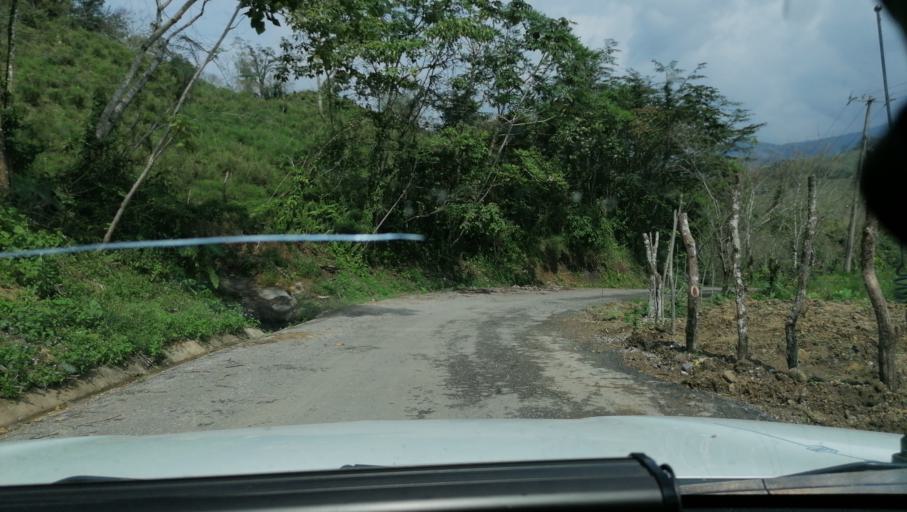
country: MX
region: Chiapas
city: Ocotepec
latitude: 17.3109
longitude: -93.1779
